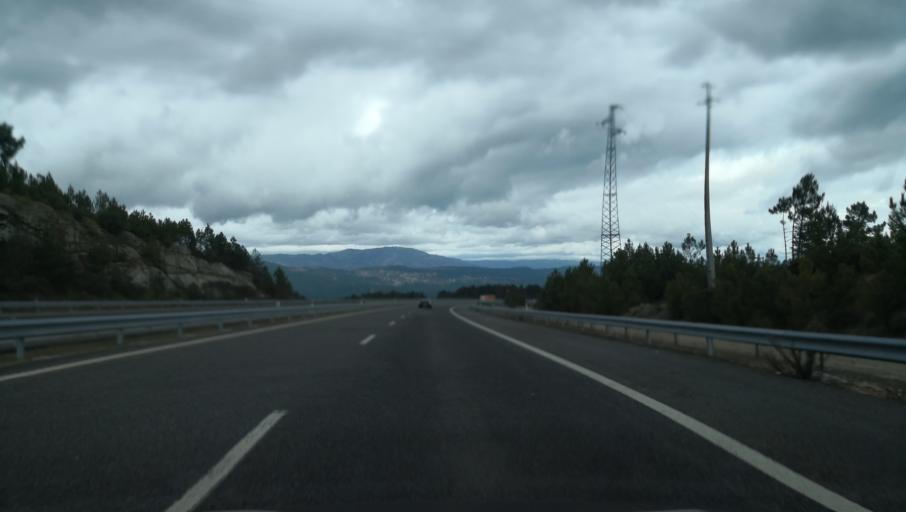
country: PT
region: Vila Real
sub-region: Boticas
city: Boticas
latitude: 41.6079
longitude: -7.6254
